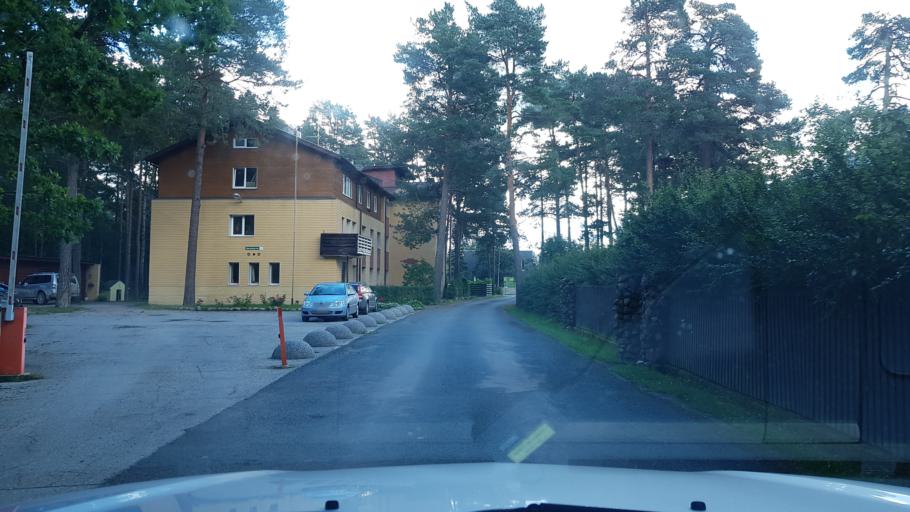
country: EE
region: Harju
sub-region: Tallinna linn
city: Tallinn
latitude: 59.3711
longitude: 24.7618
